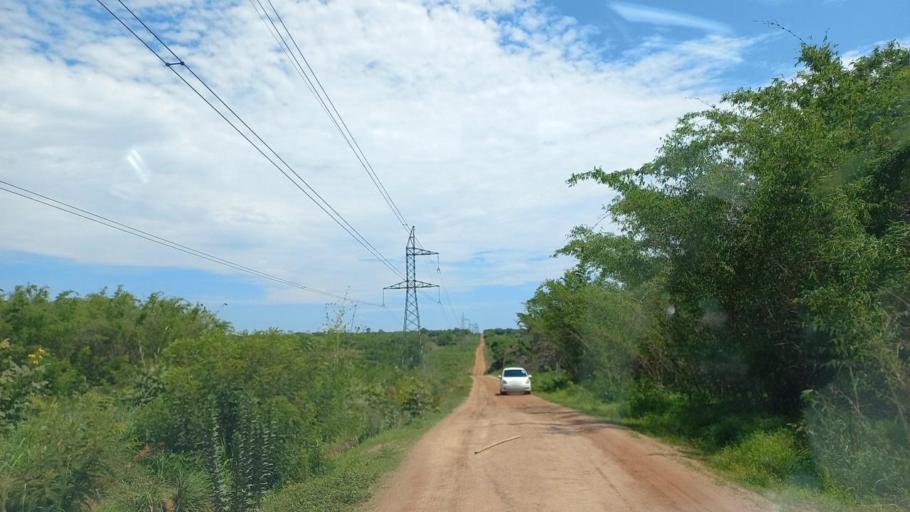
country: ZM
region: Copperbelt
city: Kitwe
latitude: -12.8150
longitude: 28.3570
